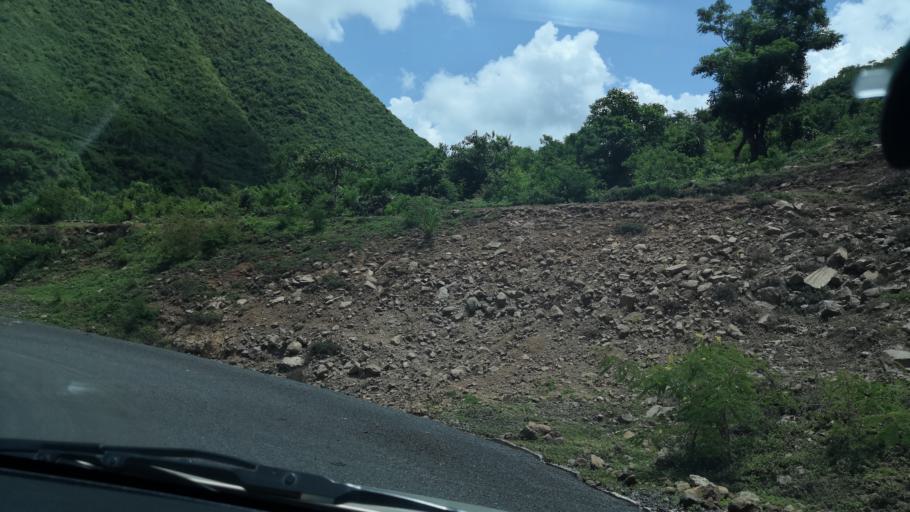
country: ET
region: Amhara
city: Abomsa
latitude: 10.3013
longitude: 39.8875
